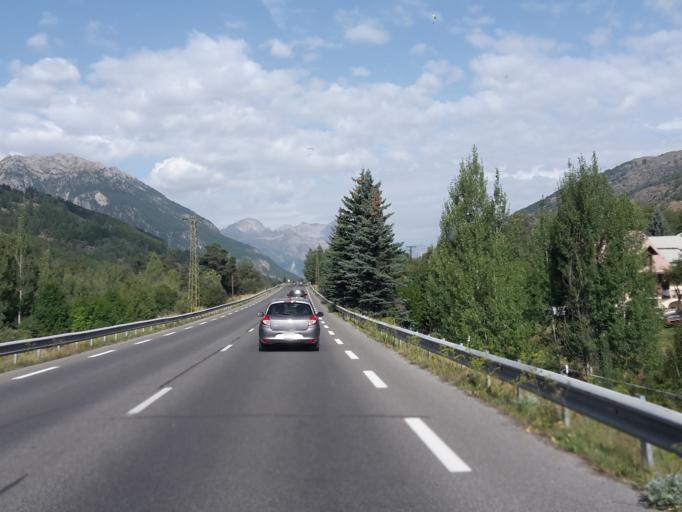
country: FR
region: Provence-Alpes-Cote d'Azur
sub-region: Departement des Hautes-Alpes
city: Saint-Chaffrey
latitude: 44.9249
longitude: 6.6055
